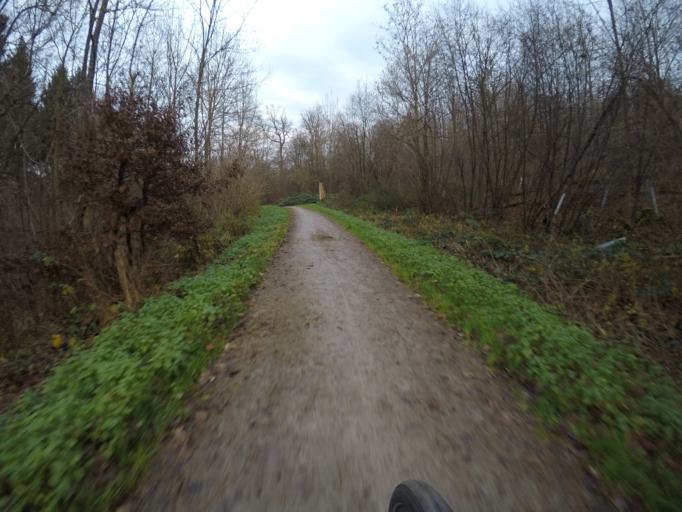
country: DE
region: Baden-Wuerttemberg
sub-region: Regierungsbezirk Stuttgart
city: Ostfildern
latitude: 48.7114
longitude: 9.2387
